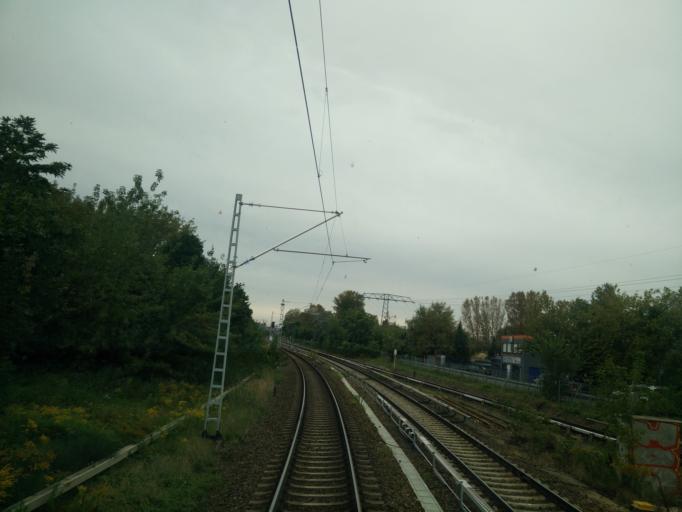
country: DE
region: Berlin
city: Rummelsburg
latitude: 52.4943
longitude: 13.4967
